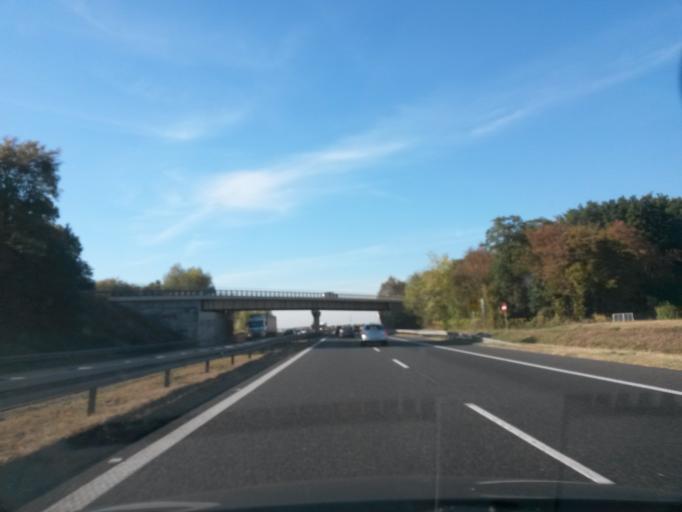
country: PL
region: Lower Silesian Voivodeship
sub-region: Powiat wroclawski
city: Zorawina
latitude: 51.0008
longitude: 17.0393
